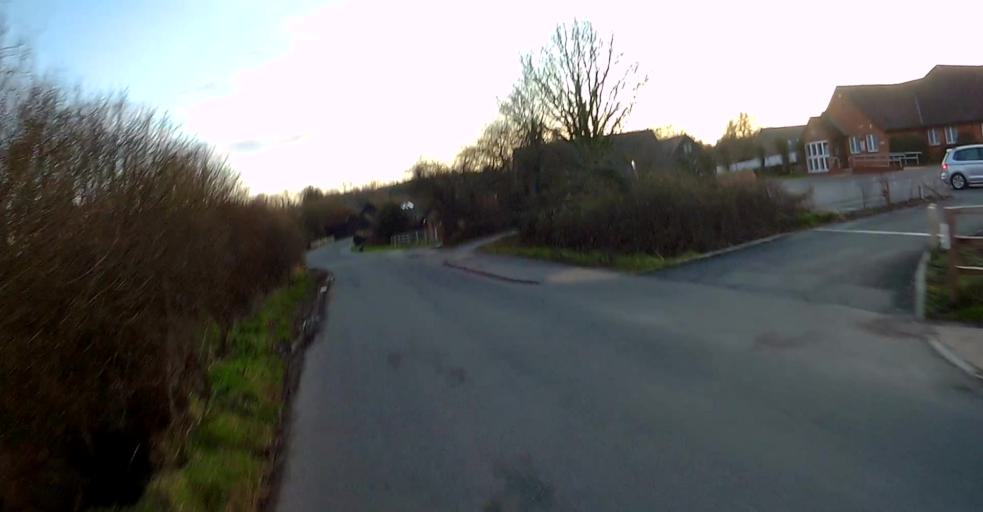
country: GB
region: England
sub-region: West Berkshire
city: Stratfield Mortimer
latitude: 51.3316
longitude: -1.0662
